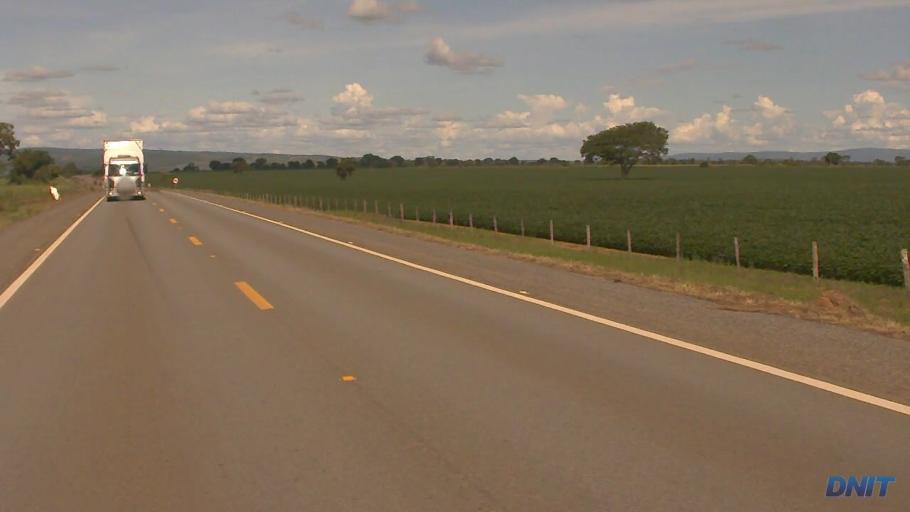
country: BR
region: Goias
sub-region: Padre Bernardo
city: Padre Bernardo
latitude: -15.2190
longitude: -48.6287
